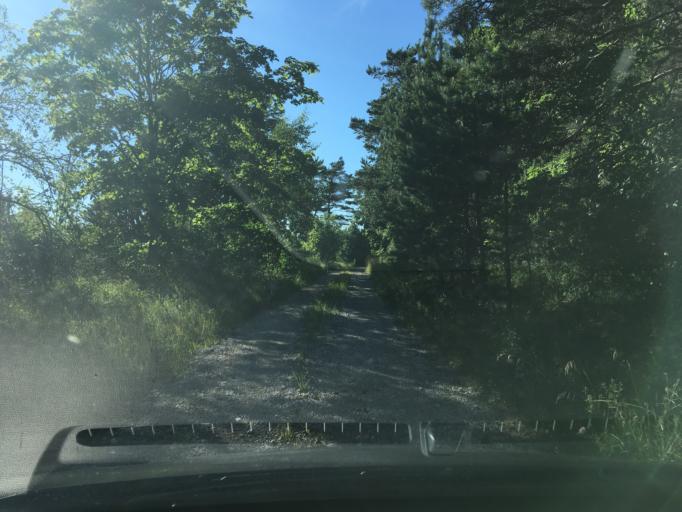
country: EE
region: Laeaene
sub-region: Lihula vald
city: Lihula
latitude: 58.5876
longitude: 23.7442
